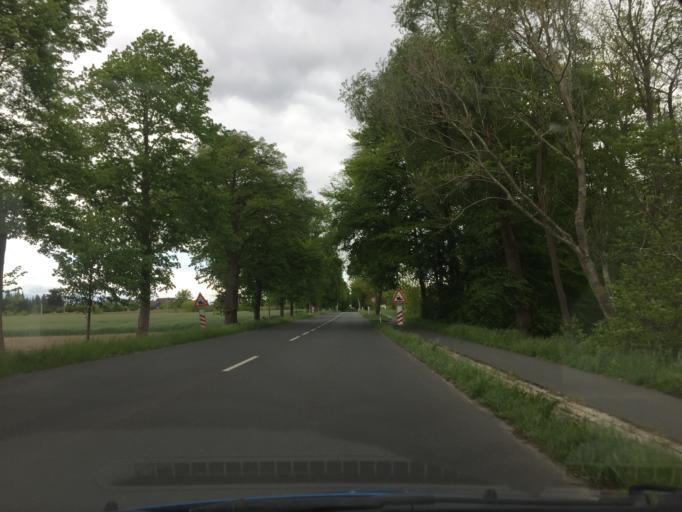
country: DE
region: Lower Saxony
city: Uelzen
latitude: 52.9443
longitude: 10.5405
